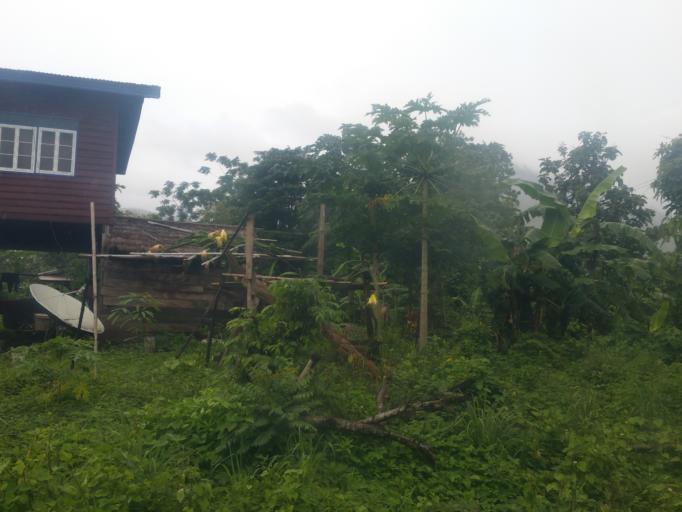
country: LA
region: Champasak
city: Pakxong
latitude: 15.3762
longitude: 106.0504
